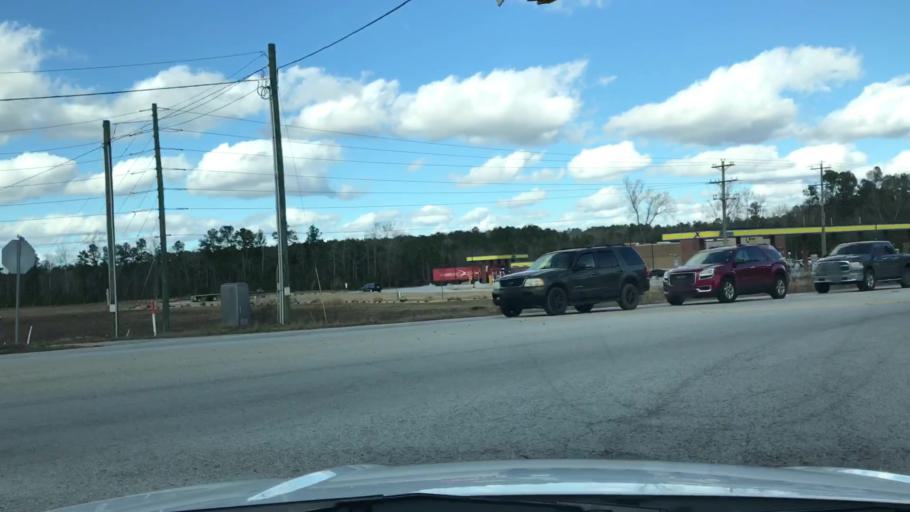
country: US
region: South Carolina
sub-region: Dorchester County
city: Summerville
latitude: 33.0826
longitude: -80.2062
